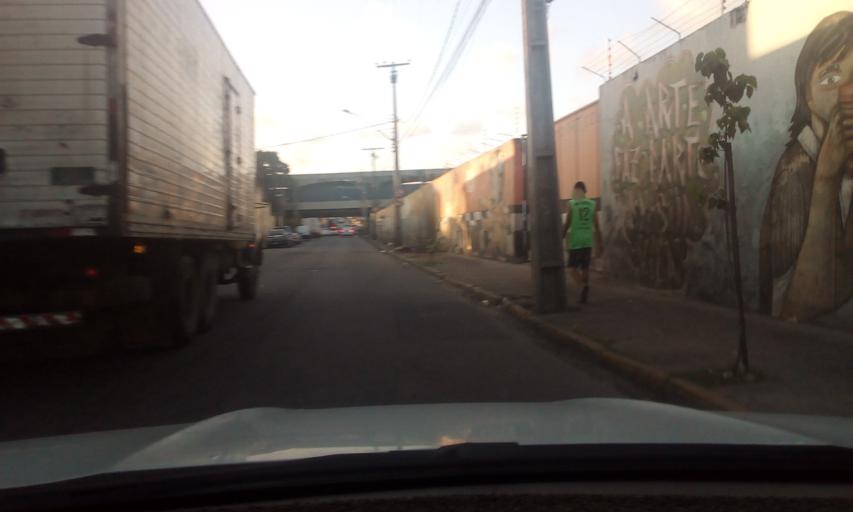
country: BR
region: Pernambuco
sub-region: Recife
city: Recife
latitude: -8.0784
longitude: -34.9053
